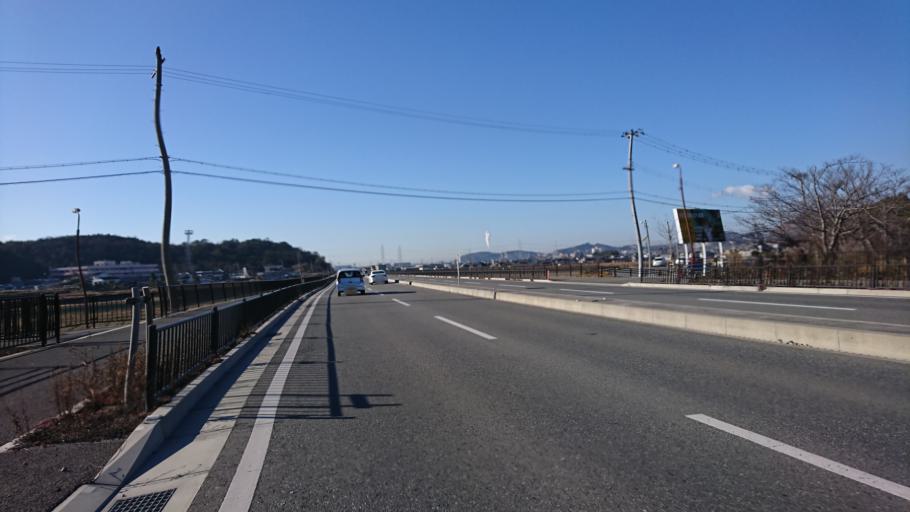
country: JP
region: Hyogo
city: Kakogawacho-honmachi
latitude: 34.8061
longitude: 134.8345
